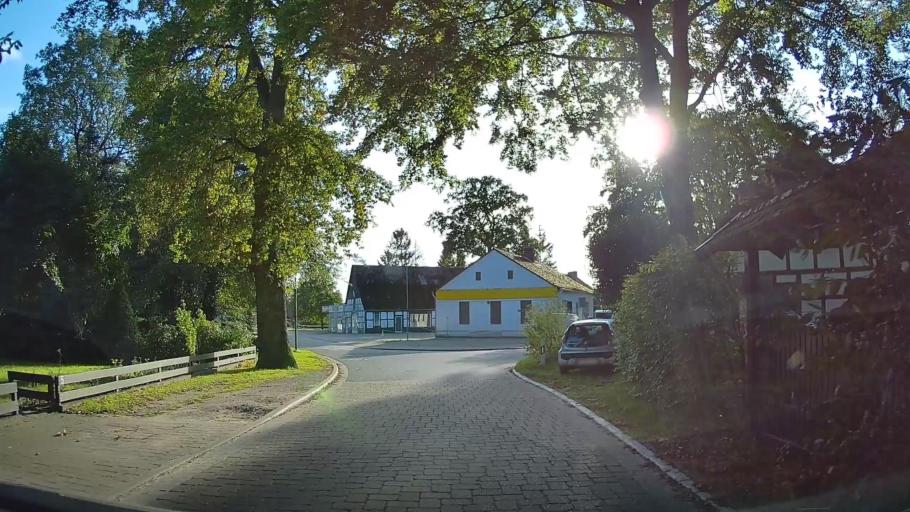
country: DE
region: Lower Saxony
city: Lauenbruck
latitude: 53.2017
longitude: 9.5461
